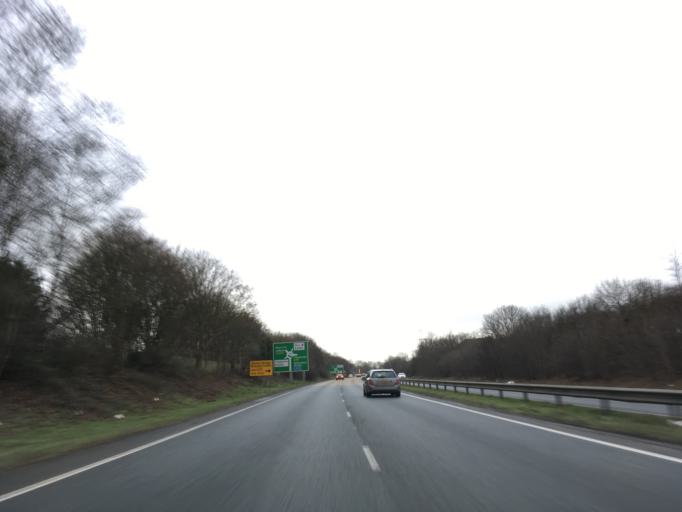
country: GB
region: England
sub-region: Gloucestershire
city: Barnwood
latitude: 51.8729
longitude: -2.1986
